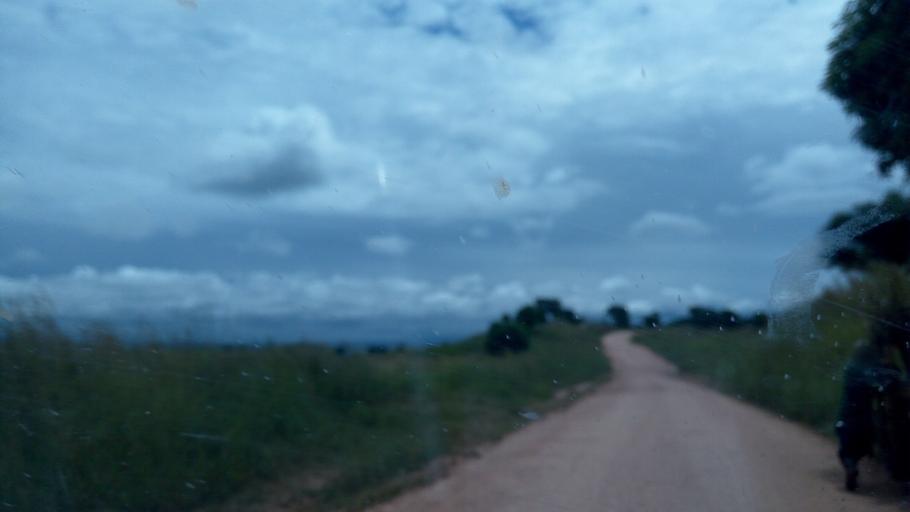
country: CD
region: Katanga
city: Kalemie
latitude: -5.9578
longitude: 29.1295
